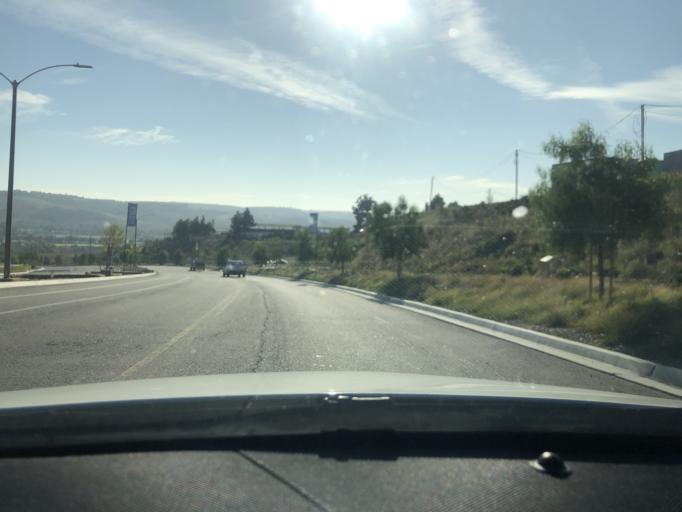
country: US
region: California
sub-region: San Diego County
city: Bonita
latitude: 32.5975
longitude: -117.0057
